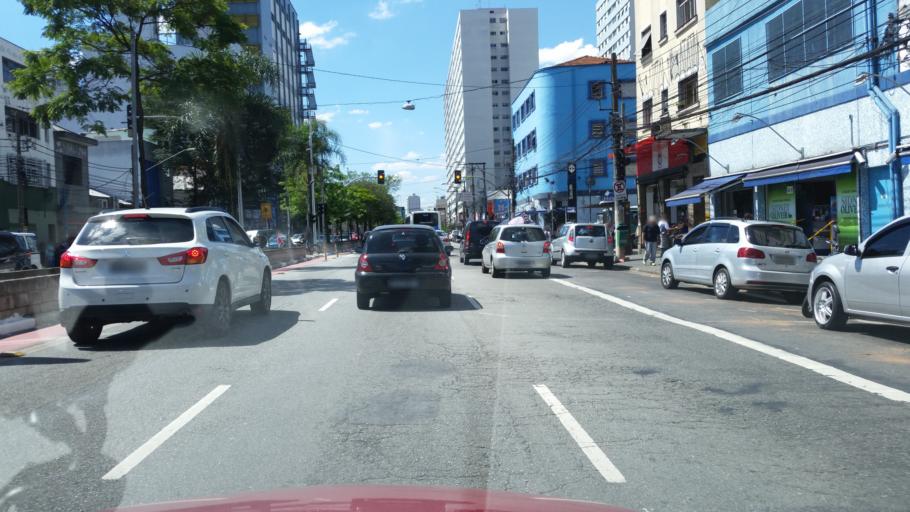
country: BR
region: Sao Paulo
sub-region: Diadema
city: Diadema
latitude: -23.6187
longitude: -46.6392
